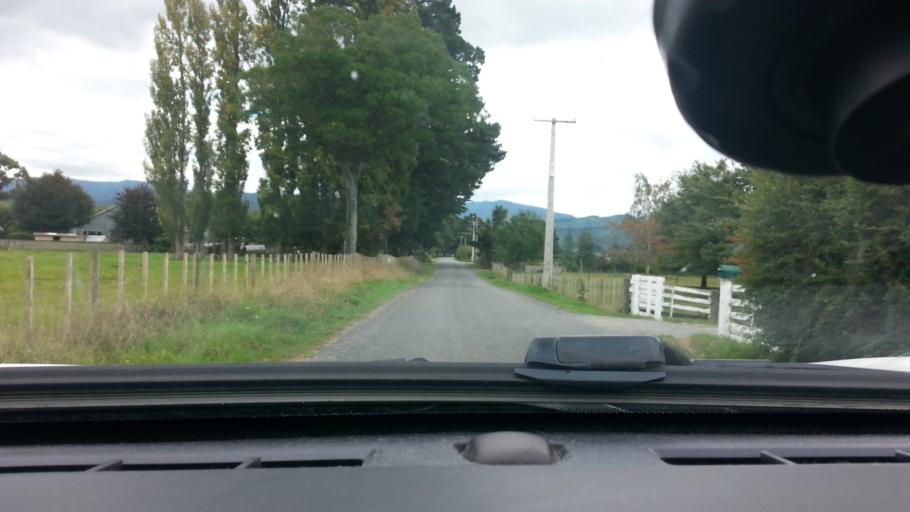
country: NZ
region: Wellington
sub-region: Masterton District
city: Masterton
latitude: -41.0681
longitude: 175.4461
